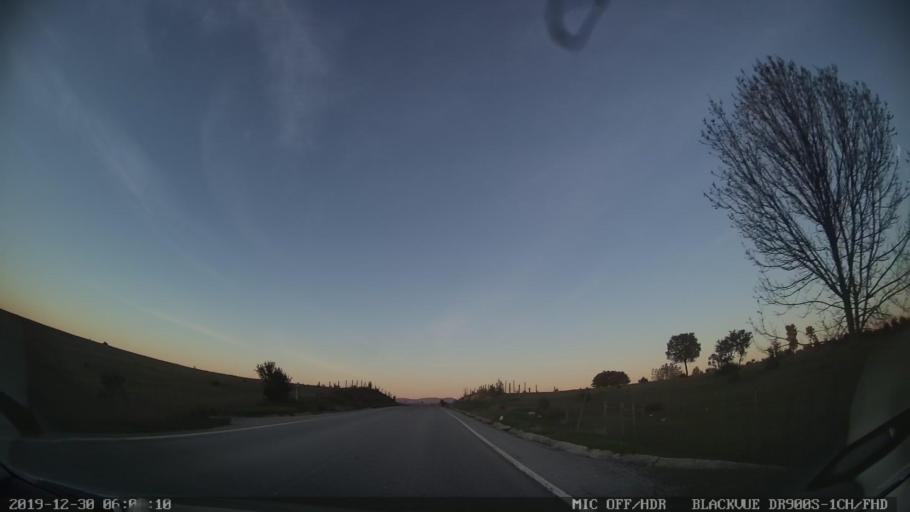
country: PT
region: Castelo Branco
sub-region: Penamacor
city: Penamacor
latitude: 40.0676
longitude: -7.2433
